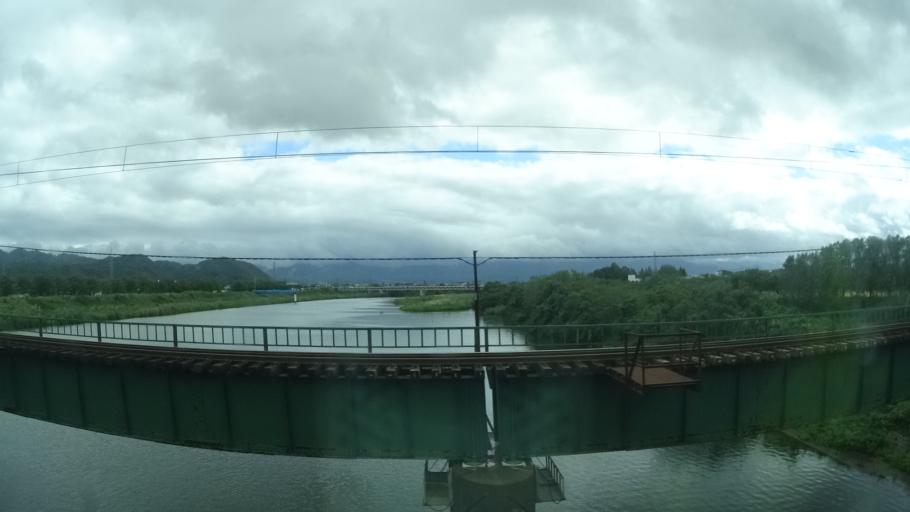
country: JP
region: Niigata
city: Shibata
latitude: 37.9639
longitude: 139.3509
